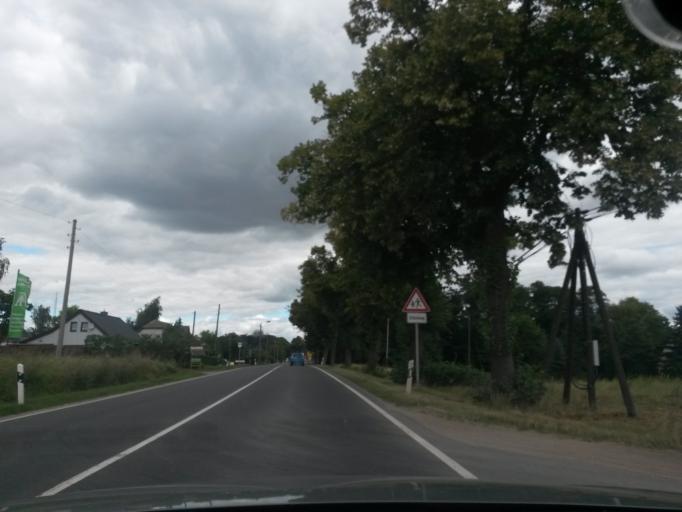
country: DE
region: Brandenburg
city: Angermunde
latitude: 52.9987
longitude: 13.9868
